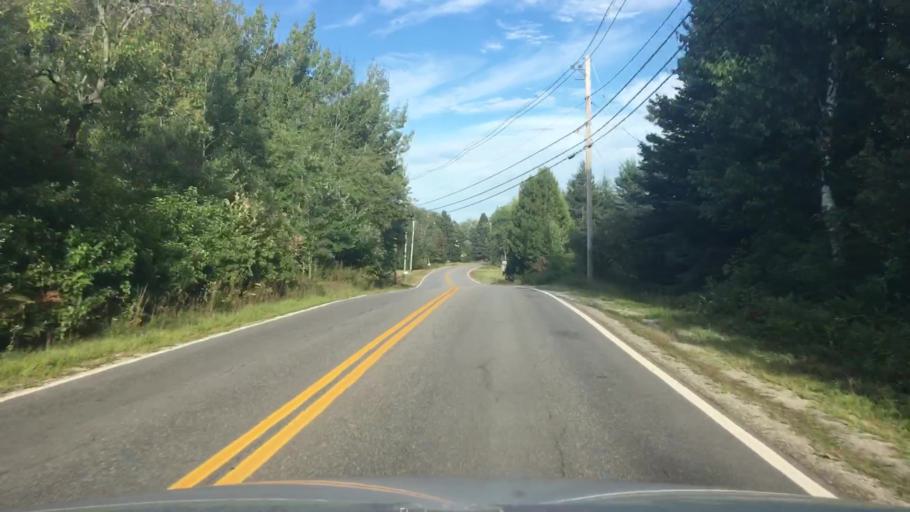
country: US
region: Maine
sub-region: Hancock County
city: Trenton
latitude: 44.4375
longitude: -68.3799
